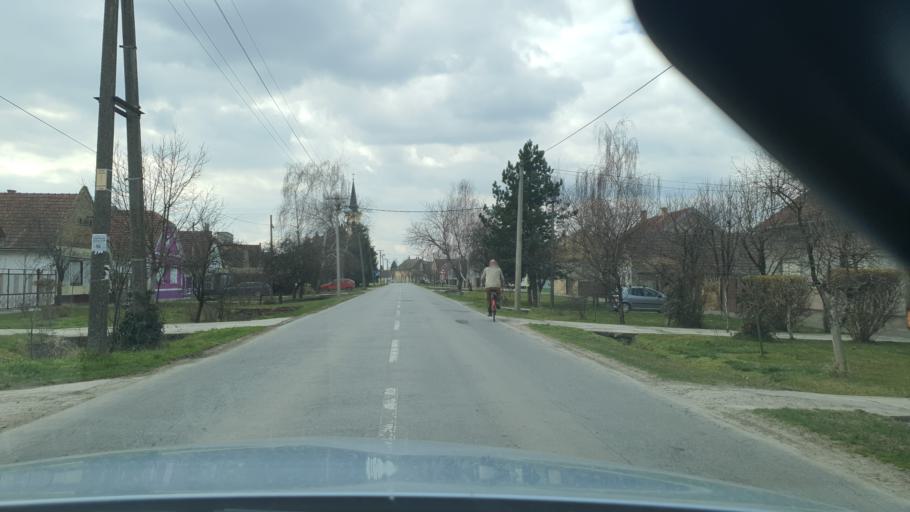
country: RS
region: Autonomna Pokrajina Vojvodina
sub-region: Juznobacki Okrug
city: Bac
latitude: 45.4089
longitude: 19.2971
